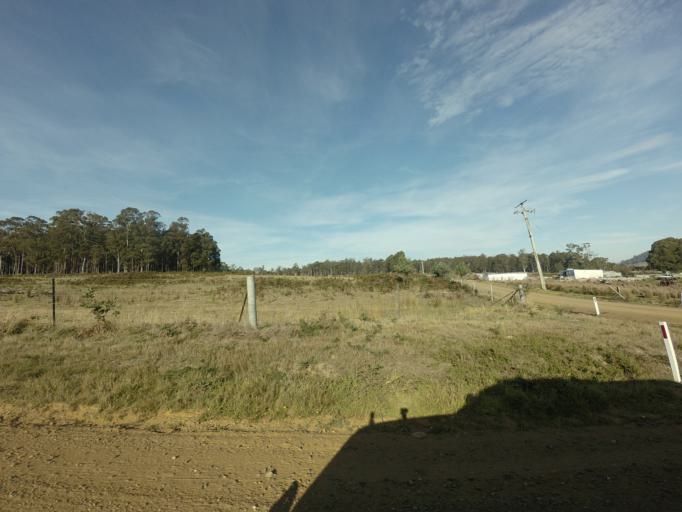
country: AU
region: Tasmania
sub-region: Brighton
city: Bridgewater
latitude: -42.4612
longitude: 147.3781
